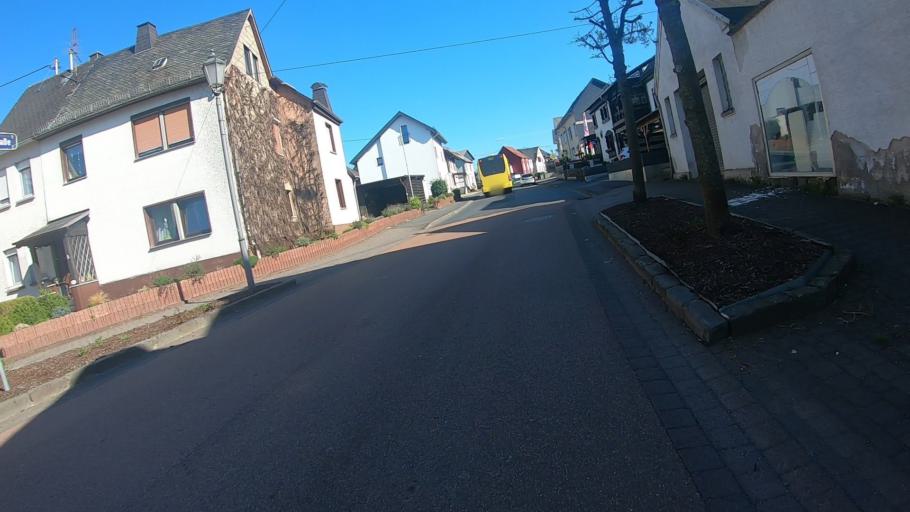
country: DE
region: Rheinland-Pfalz
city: Herschbach
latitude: 50.5725
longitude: 7.7357
